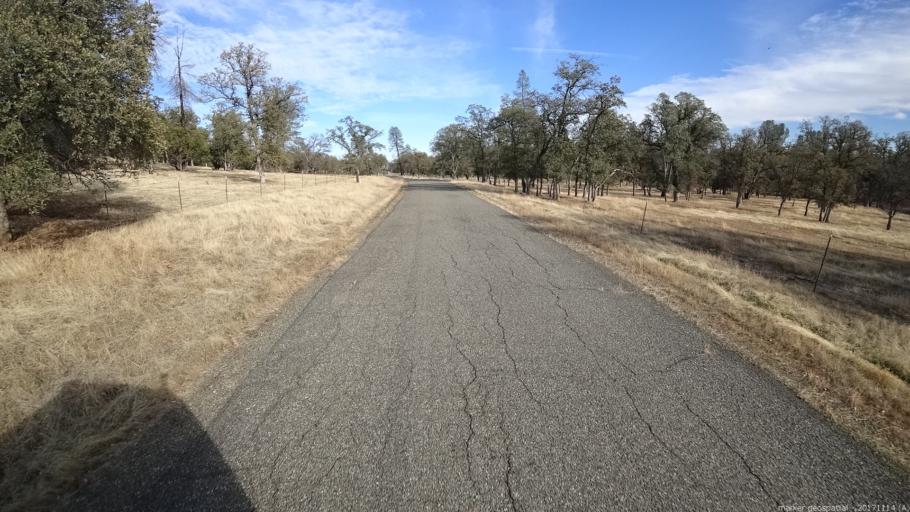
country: US
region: California
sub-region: Shasta County
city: Shasta
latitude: 40.3818
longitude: -122.5643
